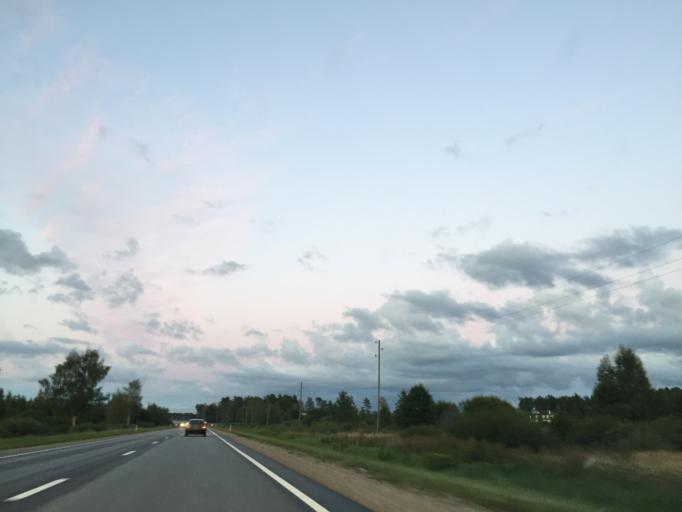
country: LV
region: Jurmala
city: Jurmala
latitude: 56.8961
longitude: 23.7232
